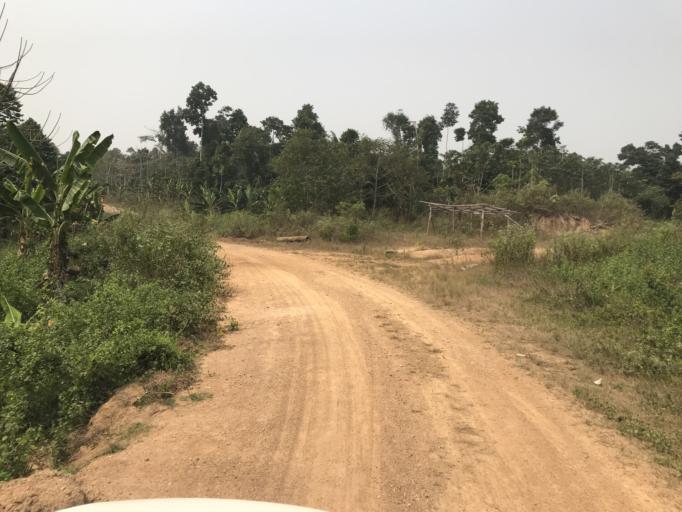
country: NG
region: Osun
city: Ifetedo
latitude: 7.0376
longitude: 4.4764
